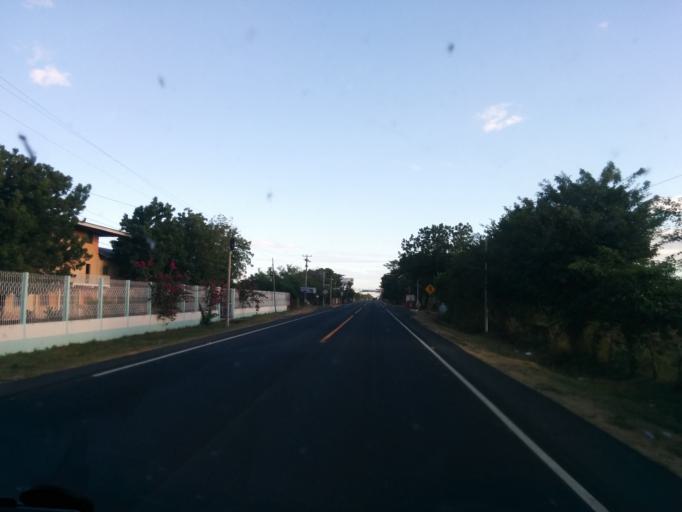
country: NI
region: Leon
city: Leon
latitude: 12.4128
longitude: -86.8646
